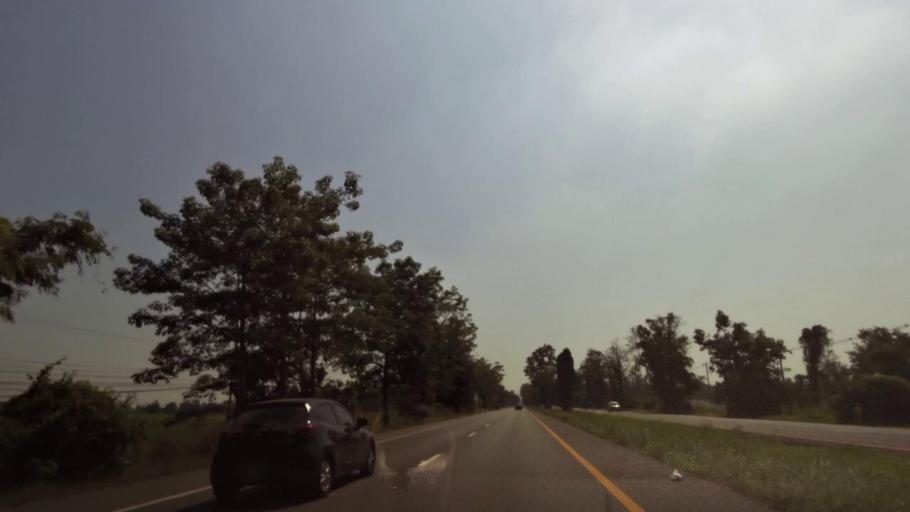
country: TH
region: Nakhon Sawan
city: Banphot Phisai
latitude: 16.0069
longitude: 100.1156
